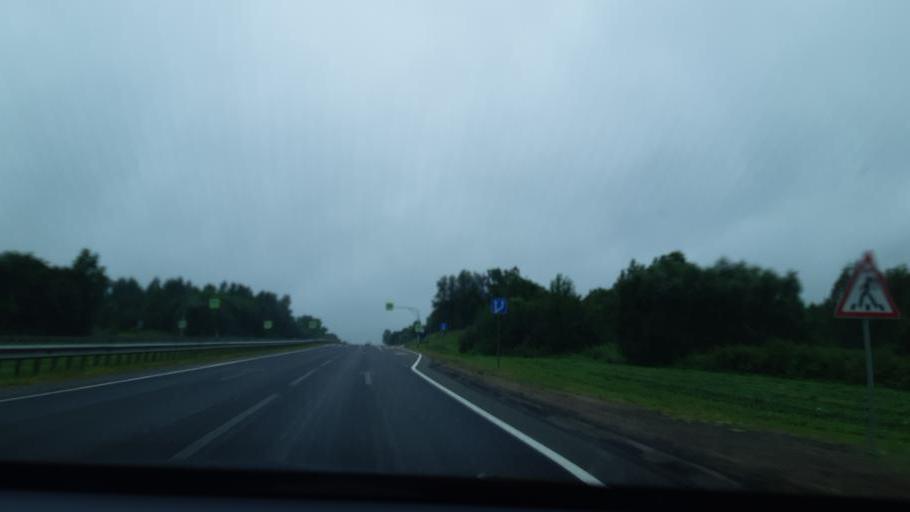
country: RU
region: Smolensk
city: Talashkino
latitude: 54.5667
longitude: 32.2432
